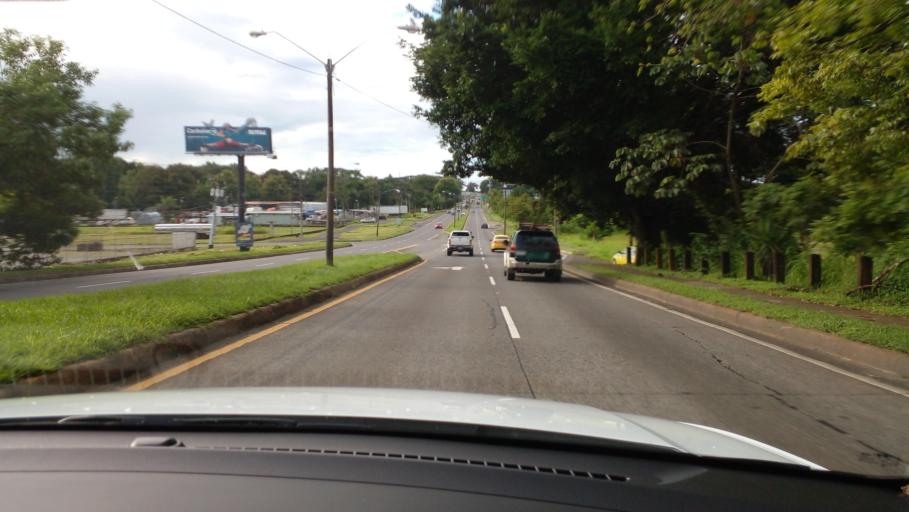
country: PA
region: Chiriqui
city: Las Lomas
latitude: 8.4396
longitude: -82.4153
